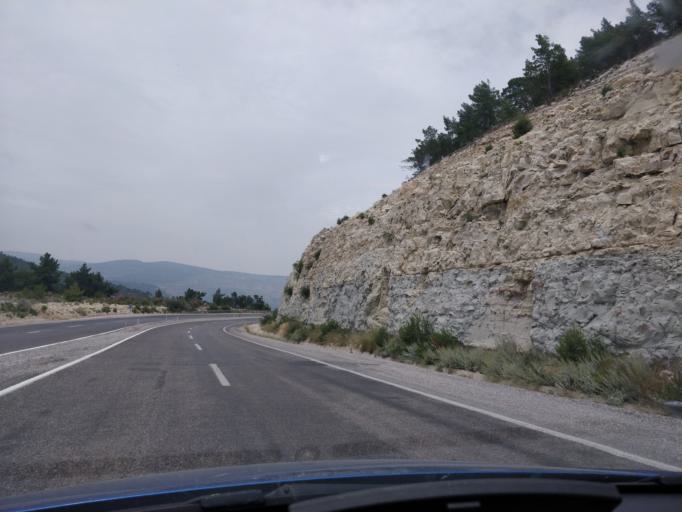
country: TR
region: Mersin
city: Tasucu
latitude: 36.3975
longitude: 33.8569
